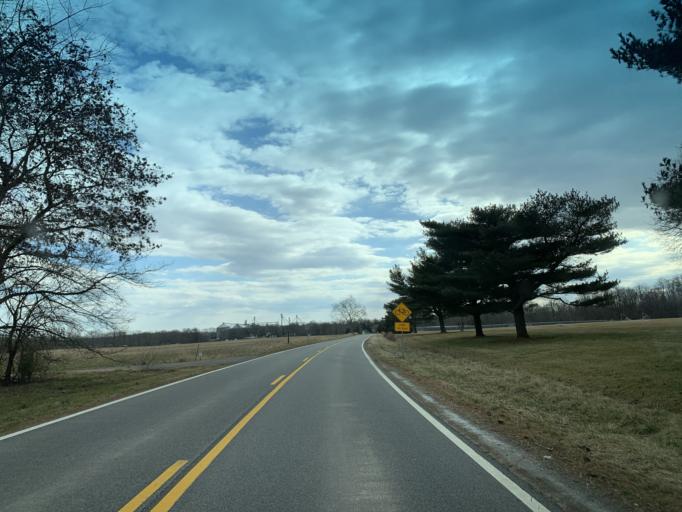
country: US
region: Maryland
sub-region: Queen Anne's County
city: Centreville
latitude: 38.9500
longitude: -76.0788
